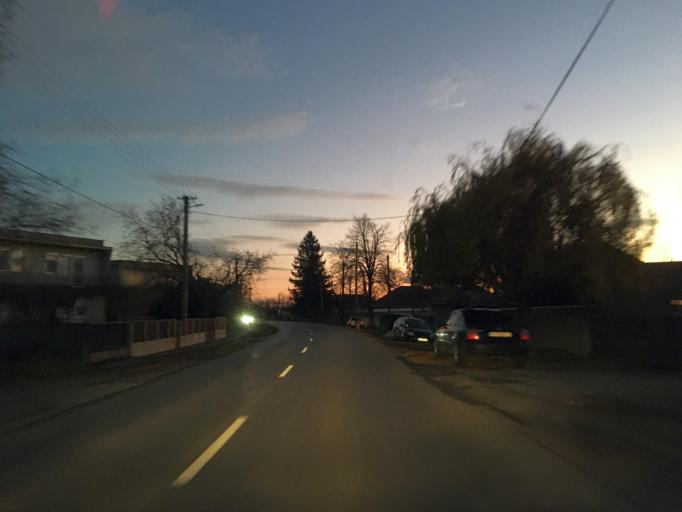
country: SK
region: Nitriansky
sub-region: Okres Komarno
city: Hurbanovo
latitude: 47.9098
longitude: 18.1354
